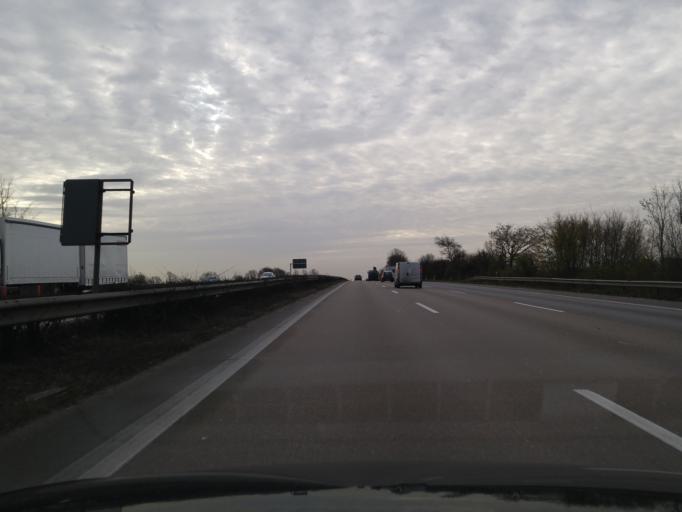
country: DE
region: Schleswig-Holstein
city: Braak
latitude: 53.6137
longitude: 10.2326
